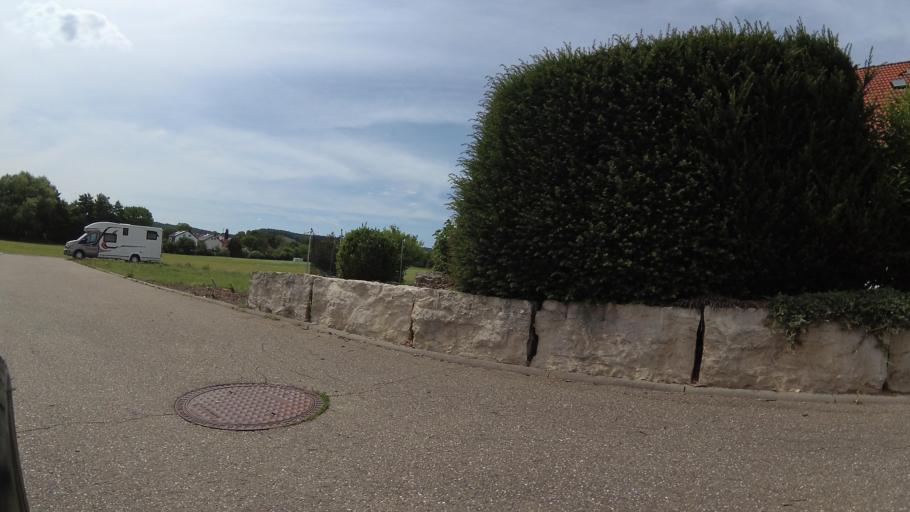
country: DE
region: Baden-Wuerttemberg
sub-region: Regierungsbezirk Stuttgart
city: Eberstadt
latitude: 49.1828
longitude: 9.3249
